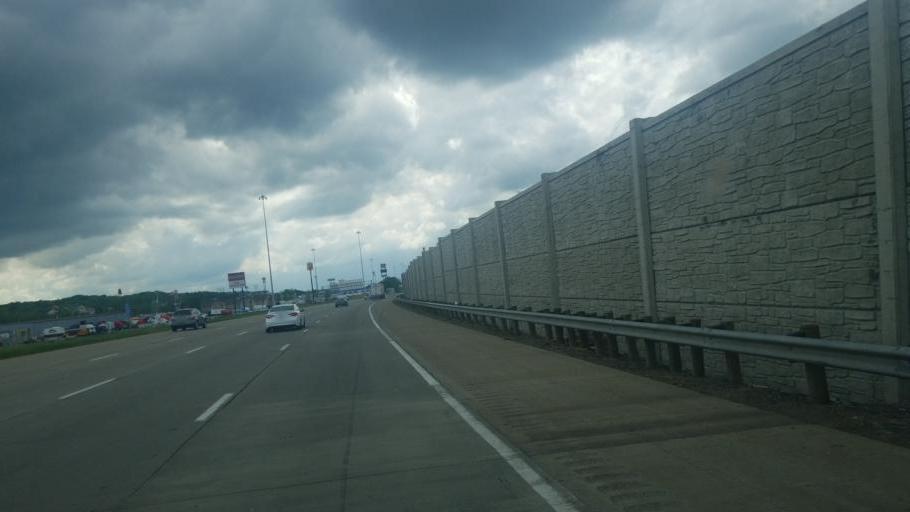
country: US
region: Ohio
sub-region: Trumbull County
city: Mineral Ridge
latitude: 41.1246
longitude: -80.7564
